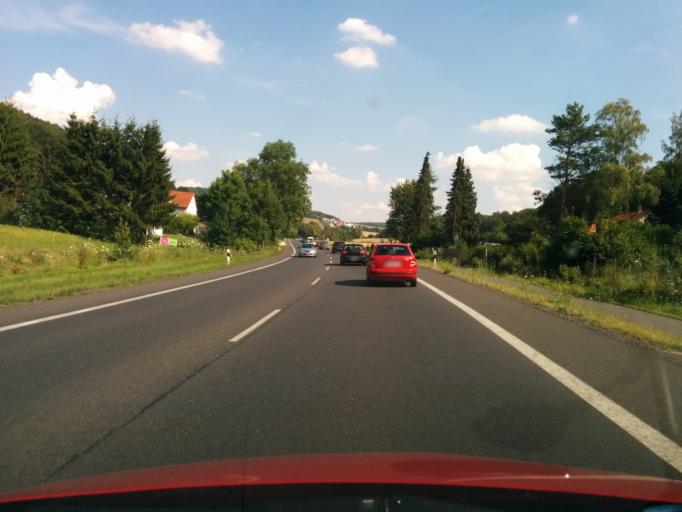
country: DE
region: Lower Saxony
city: Goettingen
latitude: 51.5519
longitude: 9.9686
